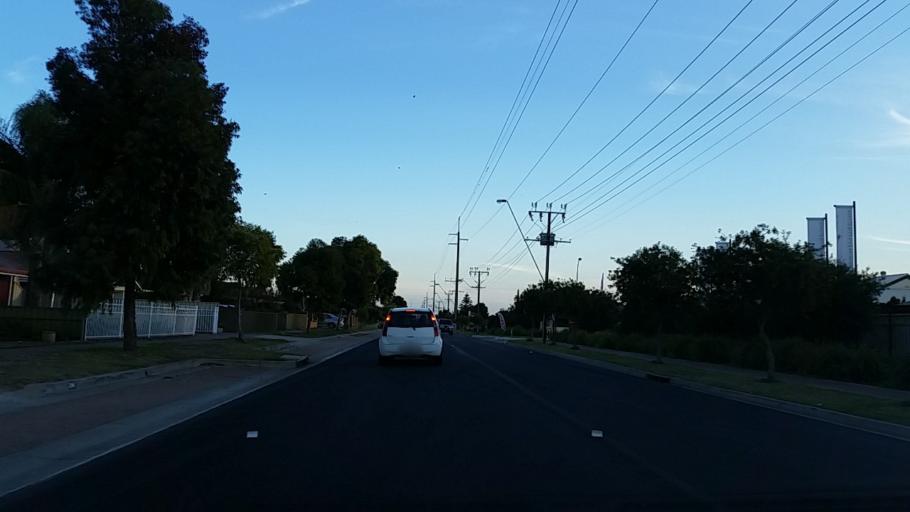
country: AU
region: South Australia
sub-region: Salisbury
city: Salisbury
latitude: -34.7841
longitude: 138.6061
